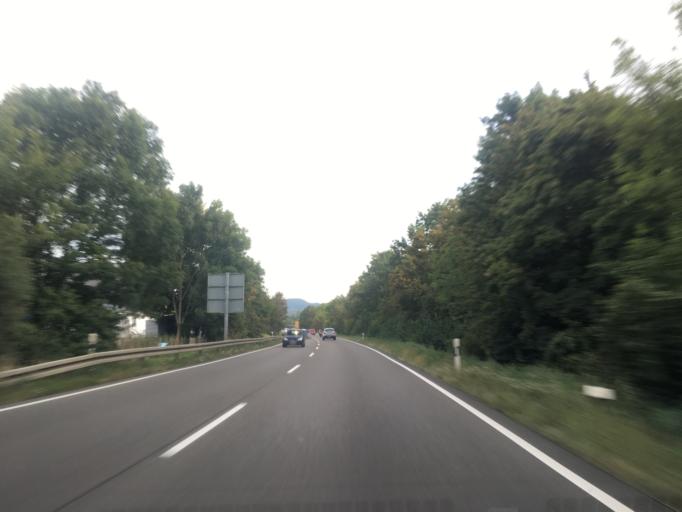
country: DE
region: Baden-Wuerttemberg
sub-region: Tuebingen Region
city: Riederich
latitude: 48.5556
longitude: 9.2601
